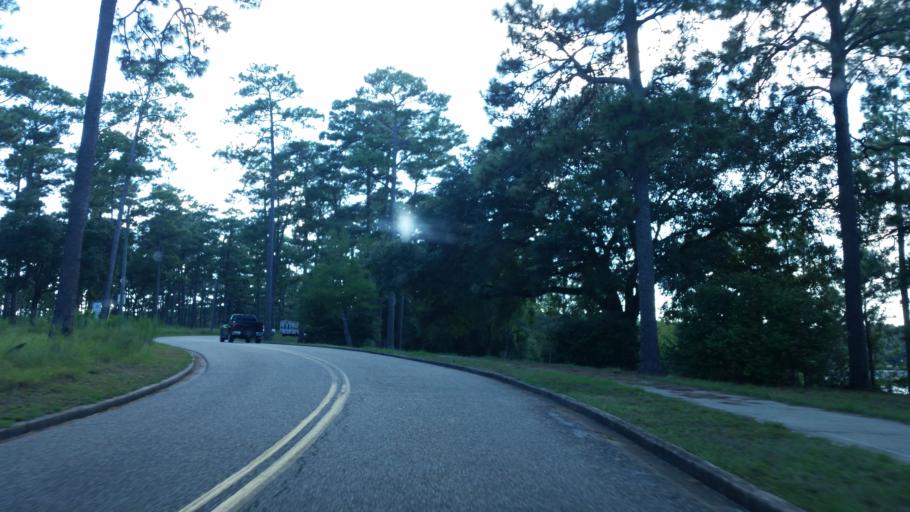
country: US
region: Alabama
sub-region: Mobile County
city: Prichard
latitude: 30.7042
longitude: -88.1587
